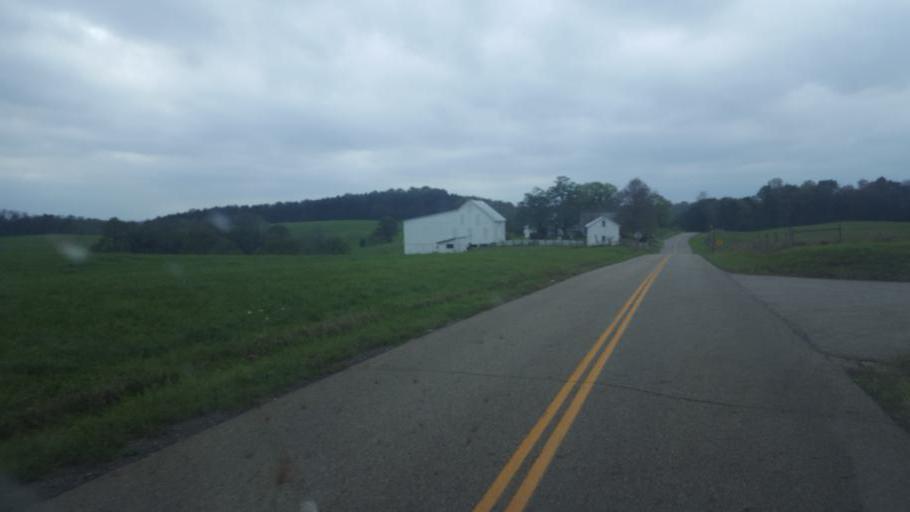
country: US
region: Ohio
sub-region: Carroll County
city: Carrollton
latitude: 40.5277
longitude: -81.1274
